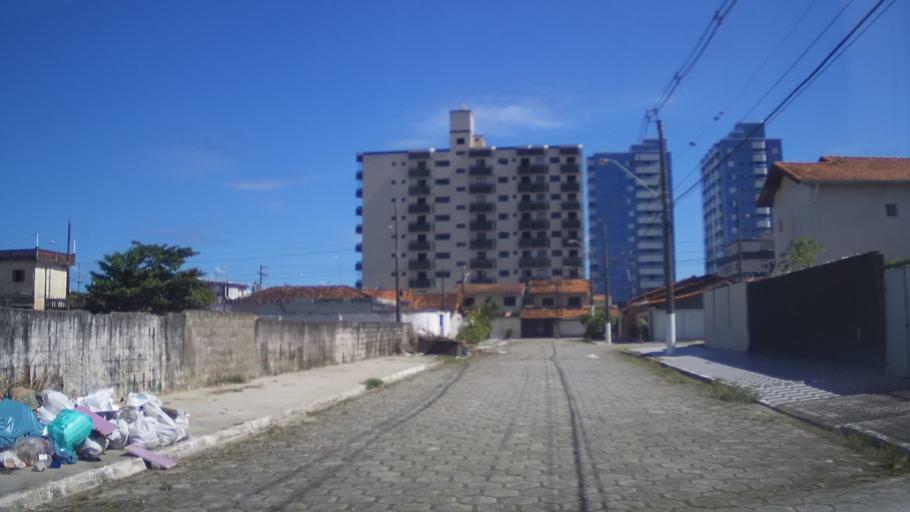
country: BR
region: Sao Paulo
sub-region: Praia Grande
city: Praia Grande
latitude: -24.0413
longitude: -46.5057
